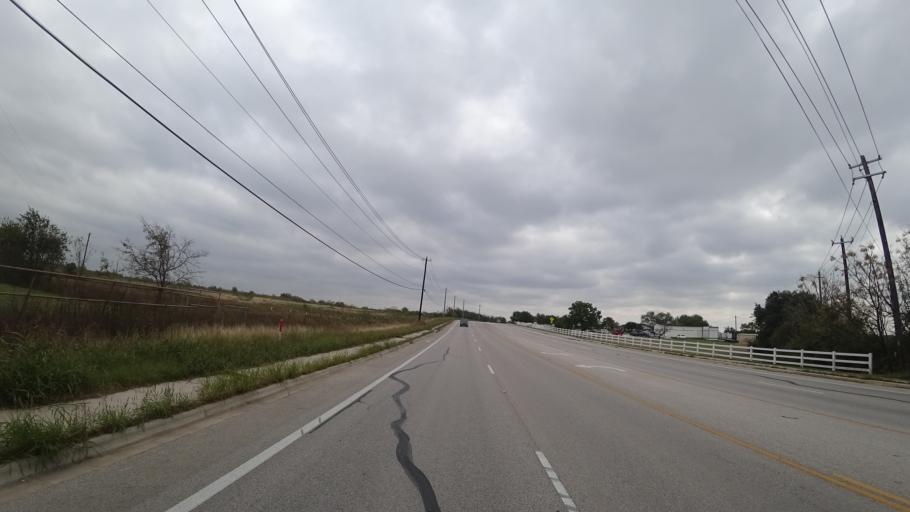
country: US
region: Texas
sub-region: Travis County
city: Pflugerville
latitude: 30.3953
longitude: -97.6305
